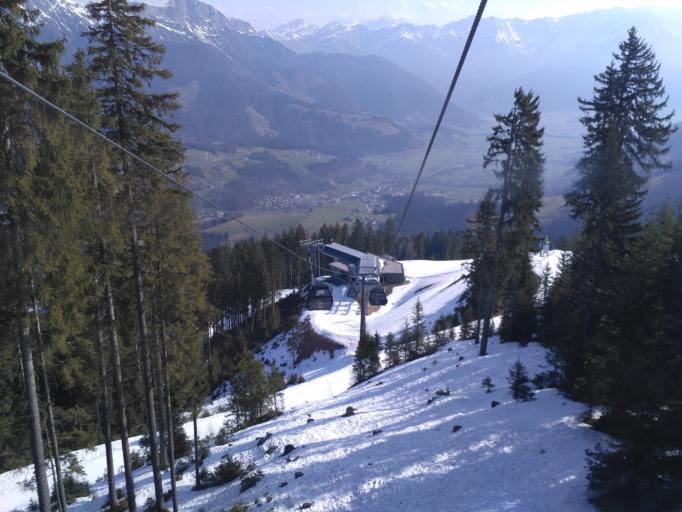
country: AT
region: Salzburg
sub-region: Politischer Bezirk Zell am See
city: Leogang
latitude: 47.4191
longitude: 12.7287
